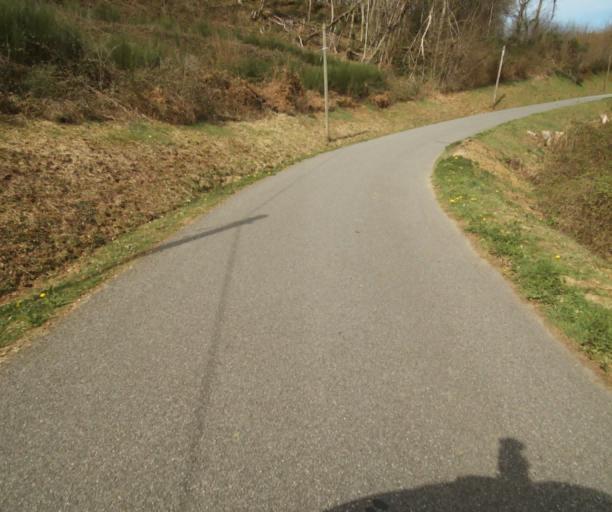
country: FR
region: Limousin
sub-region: Departement de la Correze
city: Naves
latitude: 45.3288
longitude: 1.8040
